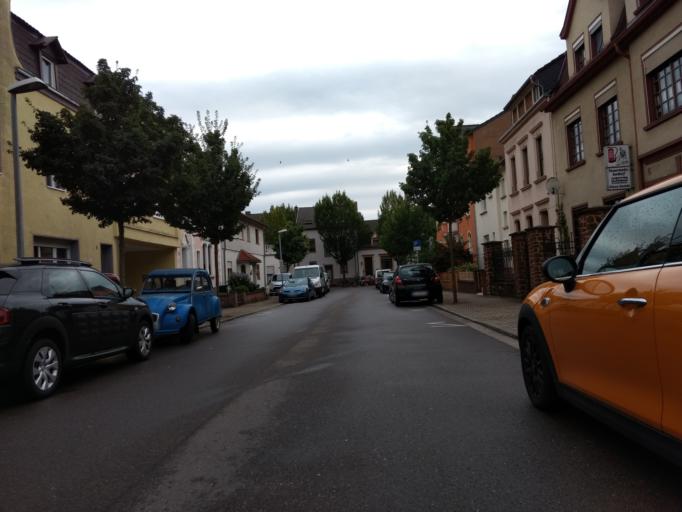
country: DE
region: Saarland
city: Dillingen
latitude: 49.3585
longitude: 6.7309
